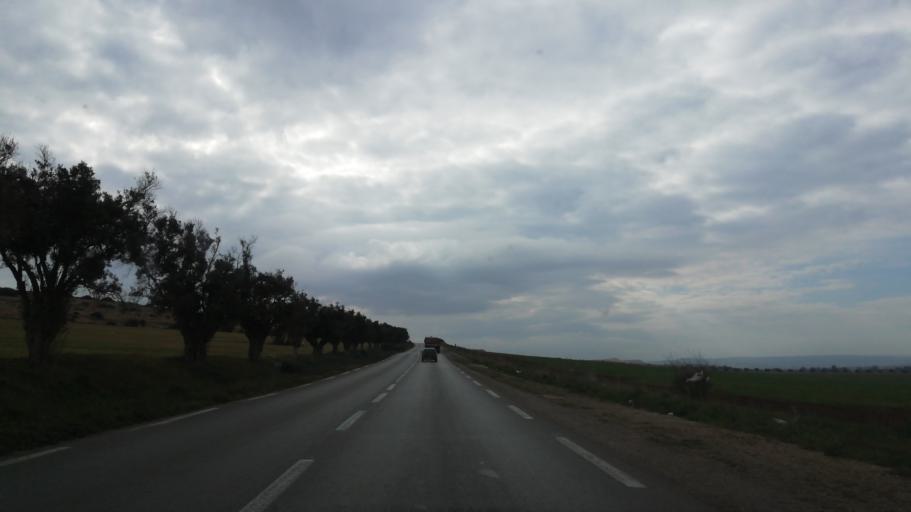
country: DZ
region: Oran
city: Ain el Bya
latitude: 35.7384
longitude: -0.3551
